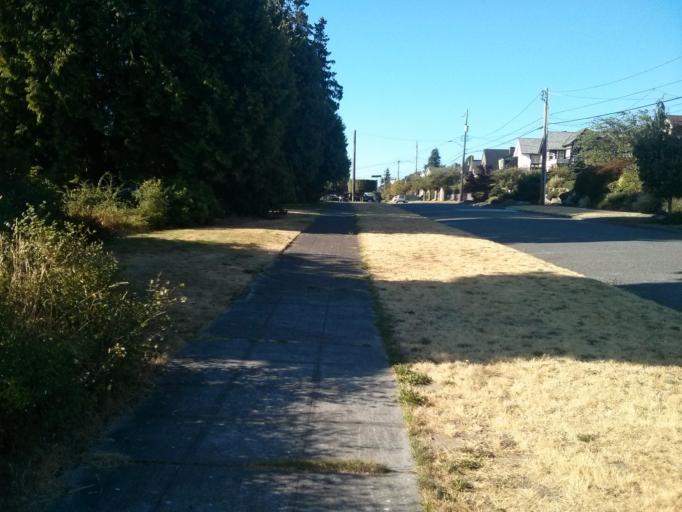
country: US
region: Washington
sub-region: King County
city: Seattle
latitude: 47.5810
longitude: -122.3779
